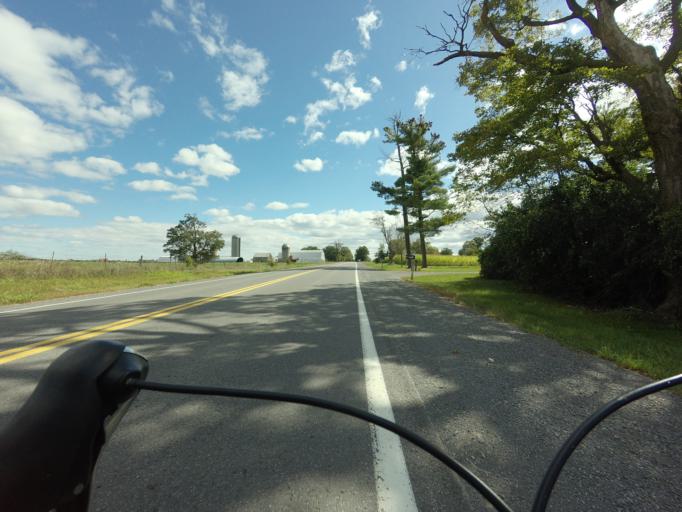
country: CA
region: Ontario
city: Bells Corners
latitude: 45.1782
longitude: -75.6649
